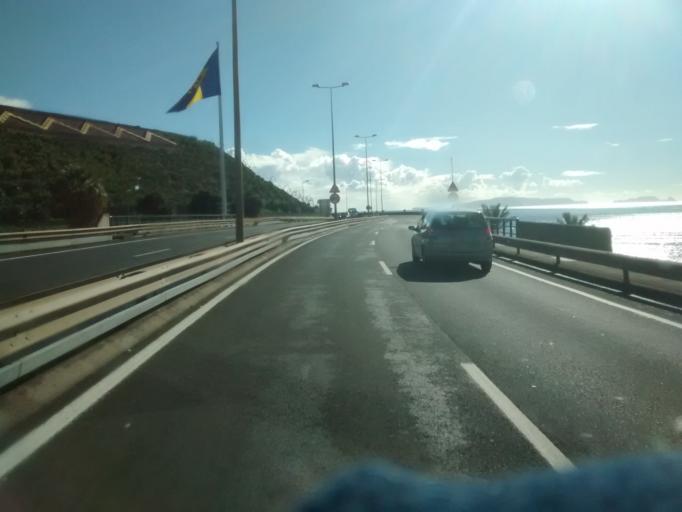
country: PT
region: Madeira
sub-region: Santa Cruz
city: Santa Cruz
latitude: 32.6888
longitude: -16.7865
